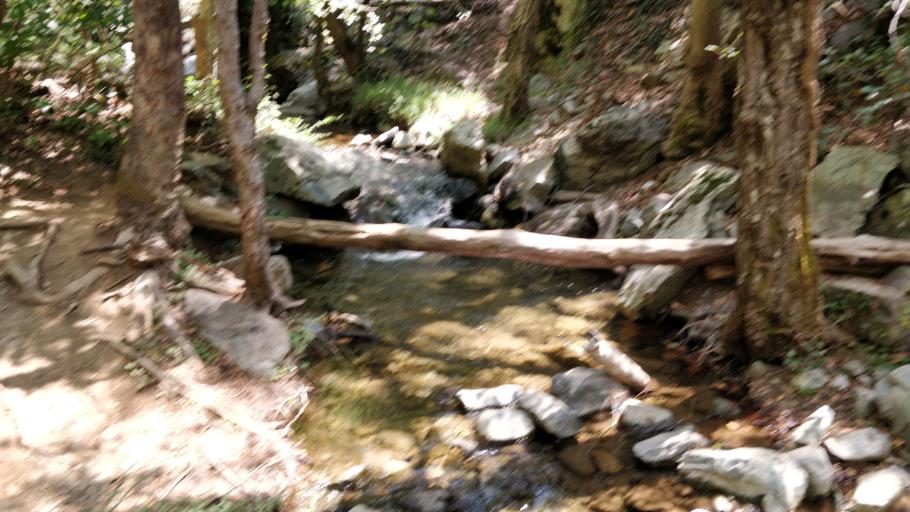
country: CY
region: Lefkosia
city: Kakopetria
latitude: 34.9001
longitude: 32.8698
